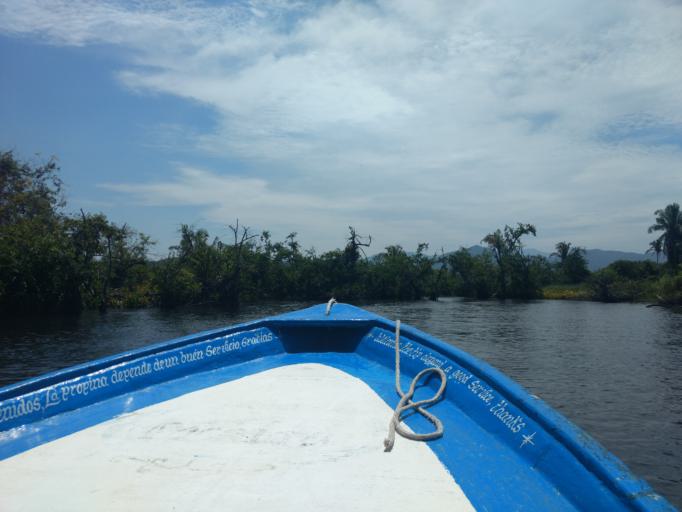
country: MX
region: Nayarit
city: San Blas
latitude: 21.5351
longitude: -105.2376
